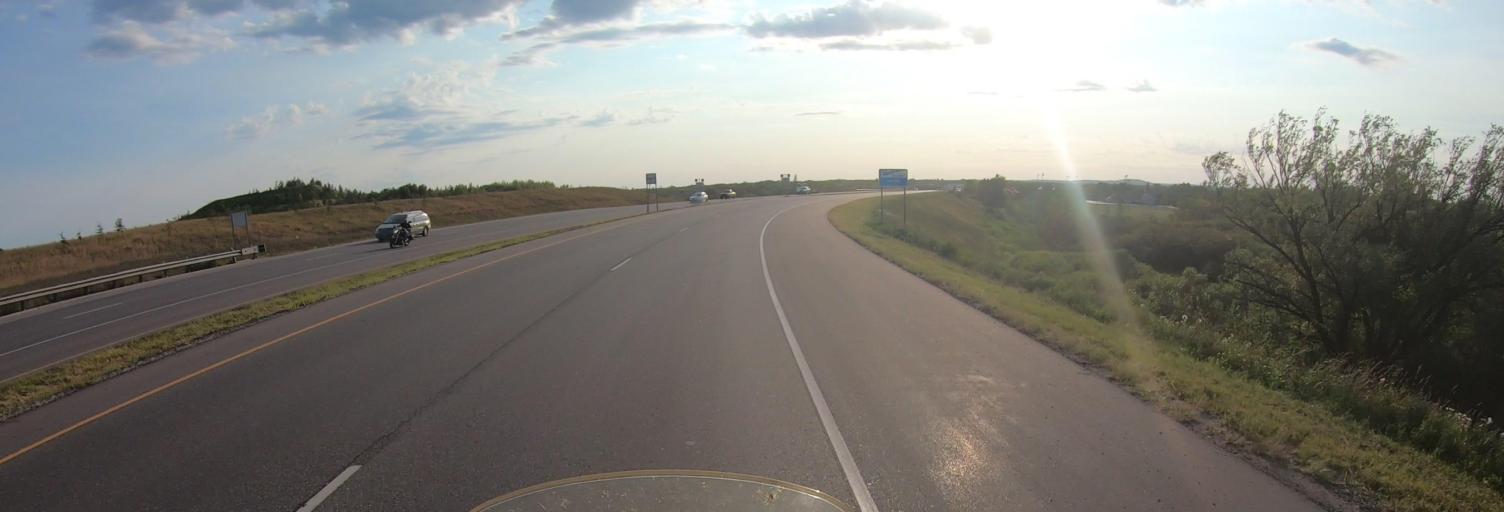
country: US
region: Minnesota
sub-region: Saint Louis County
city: Virginia
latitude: 47.5103
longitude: -92.5338
